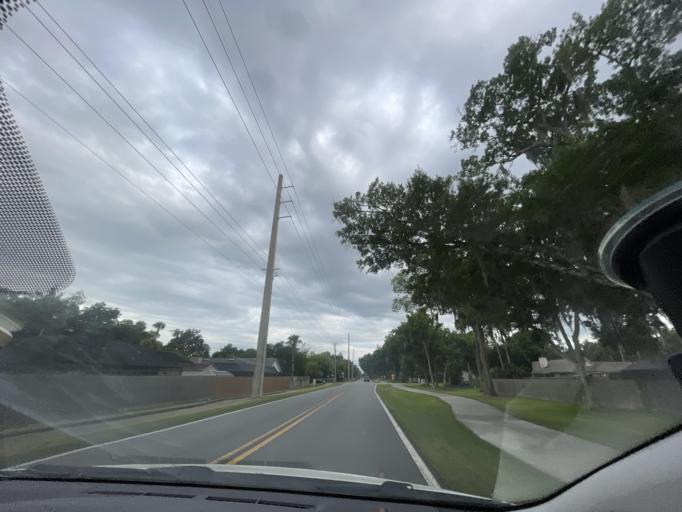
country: US
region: Florida
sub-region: Volusia County
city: Port Orange
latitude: 29.0984
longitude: -80.9931
